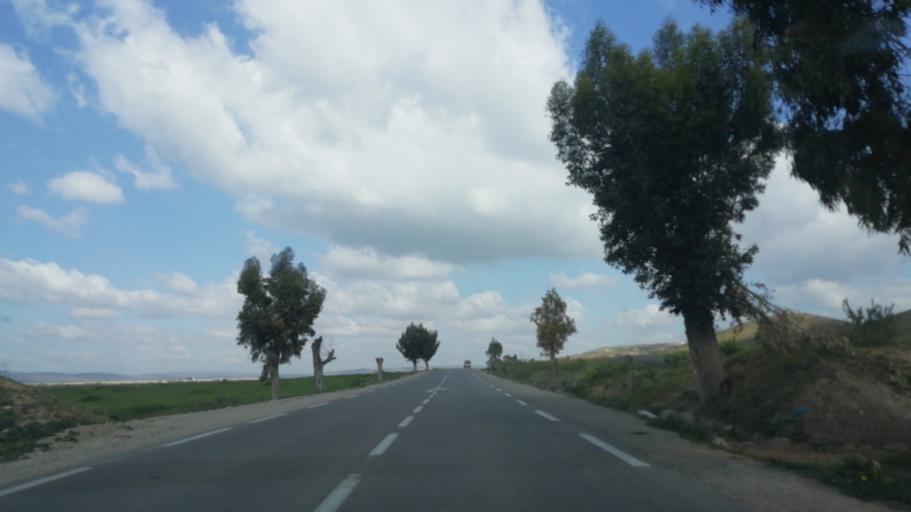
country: DZ
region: Mostaganem
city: Mostaganem
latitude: 35.6982
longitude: 0.2183
